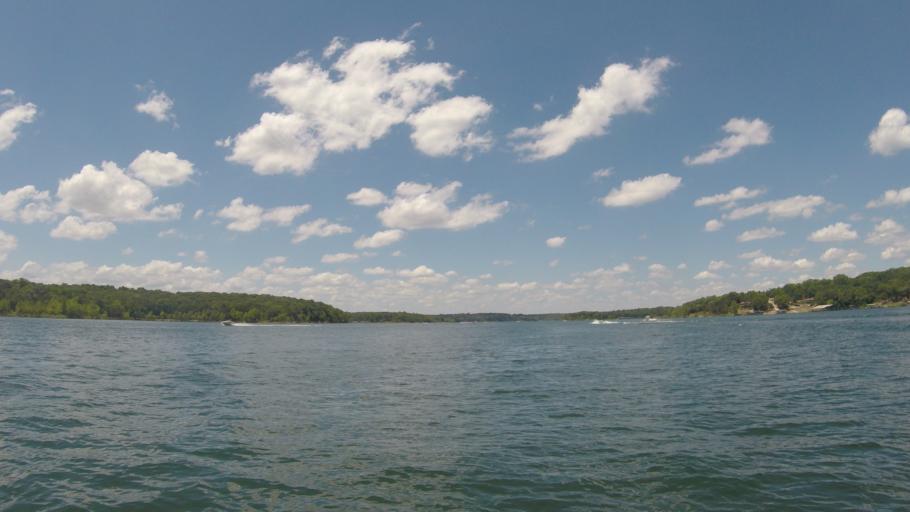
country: US
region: Missouri
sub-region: Barry County
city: Shell Knob
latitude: 36.5898
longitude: -93.5507
